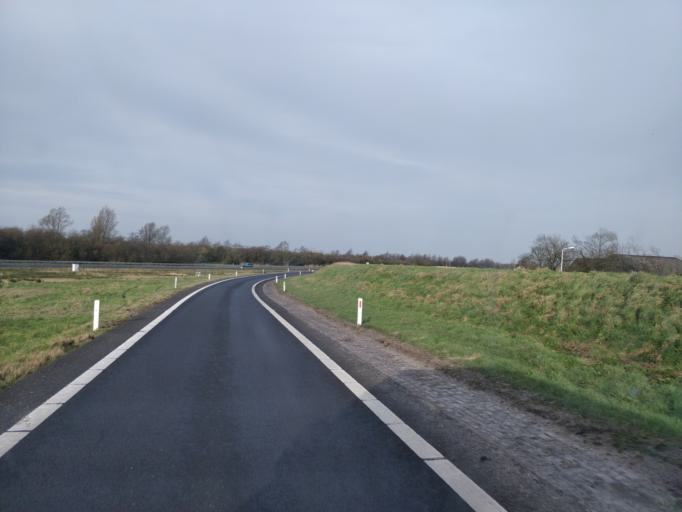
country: NL
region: Friesland
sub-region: Gemeente Boarnsterhim
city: Reduzum
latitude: 53.1139
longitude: 5.8135
